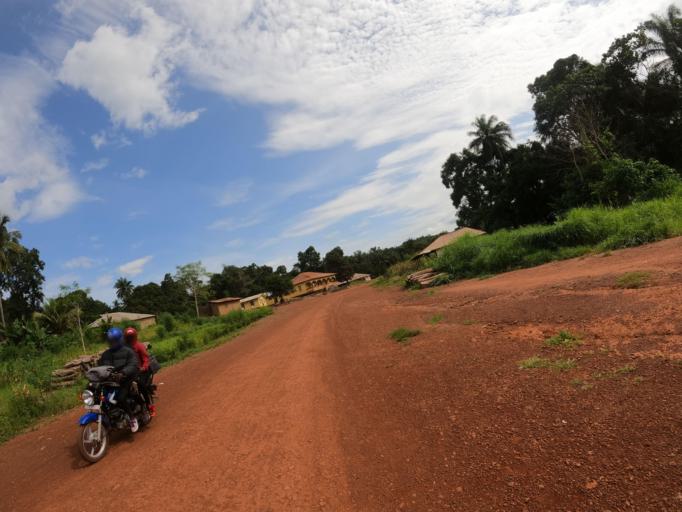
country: SL
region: Northern Province
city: Kamakwie
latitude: 9.2107
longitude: -12.2024
